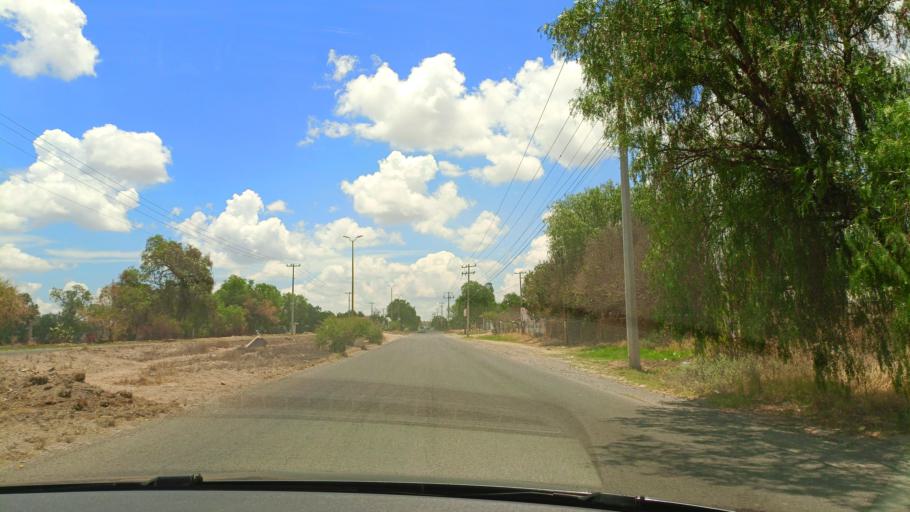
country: MX
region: Guanajuato
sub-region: San Luis de la Paz
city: San Ignacio
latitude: 21.2875
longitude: -100.5457
